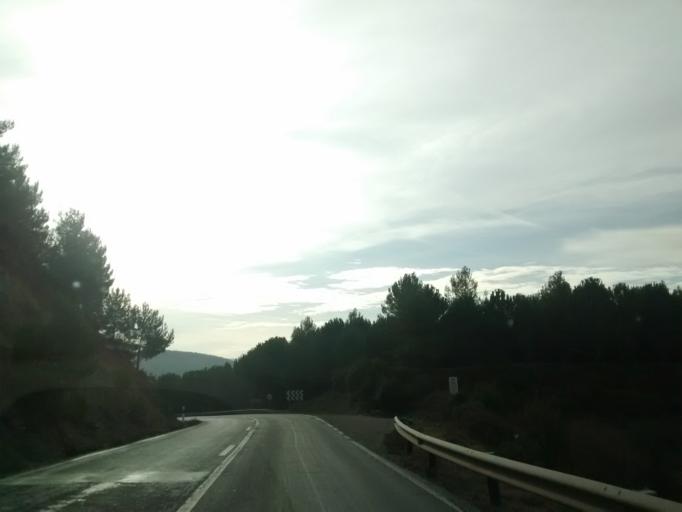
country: ES
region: Aragon
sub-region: Provincia de Zaragoza
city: Undues de Lerda
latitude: 42.6105
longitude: -1.0975
